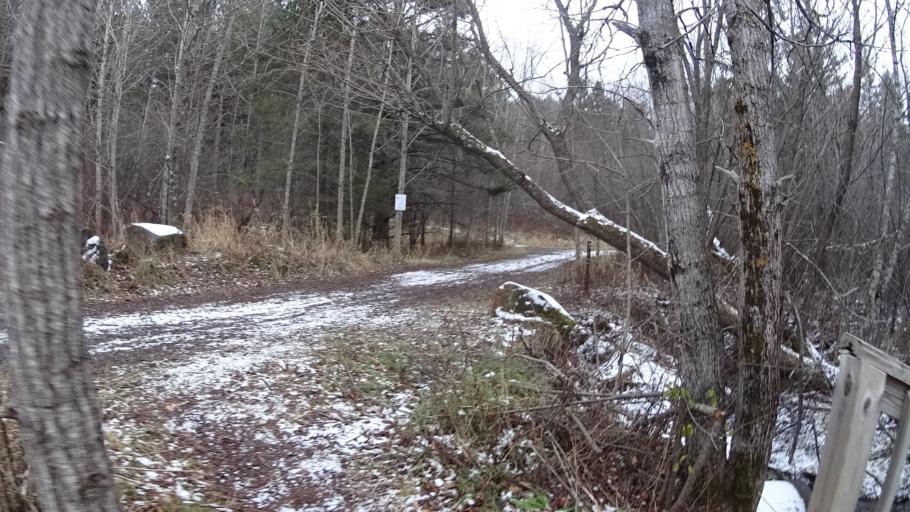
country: US
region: Minnesota
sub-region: Saint Louis County
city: Arnold
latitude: 46.8383
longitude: -92.0821
